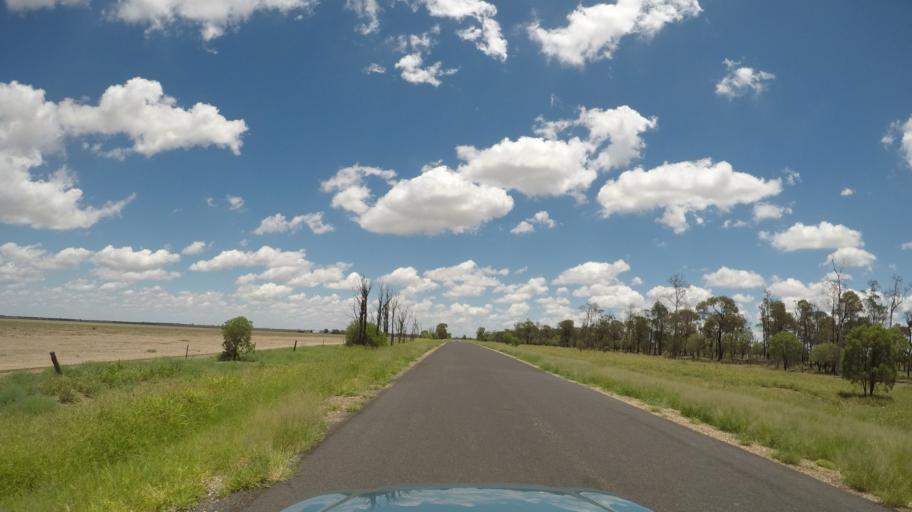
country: AU
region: Queensland
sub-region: Goondiwindi
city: Goondiwindi
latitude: -28.1620
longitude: 150.1447
